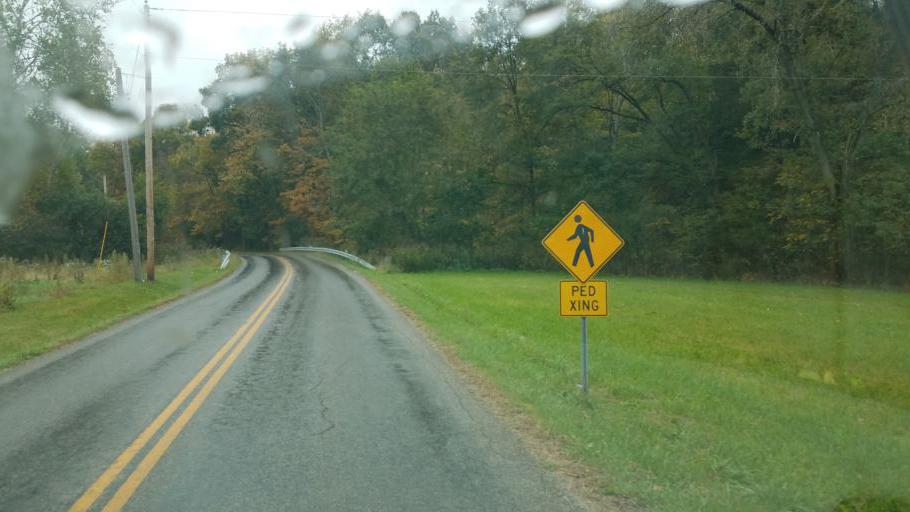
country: US
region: Ohio
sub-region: Holmes County
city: Millersburg
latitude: 40.5748
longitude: -81.8723
